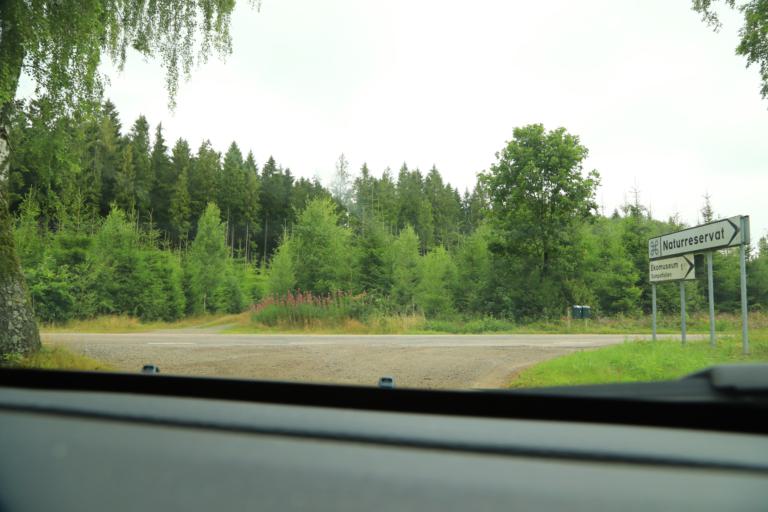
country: SE
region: Halland
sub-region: Falkenbergs Kommun
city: Falkenberg
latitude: 57.0969
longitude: 12.6686
